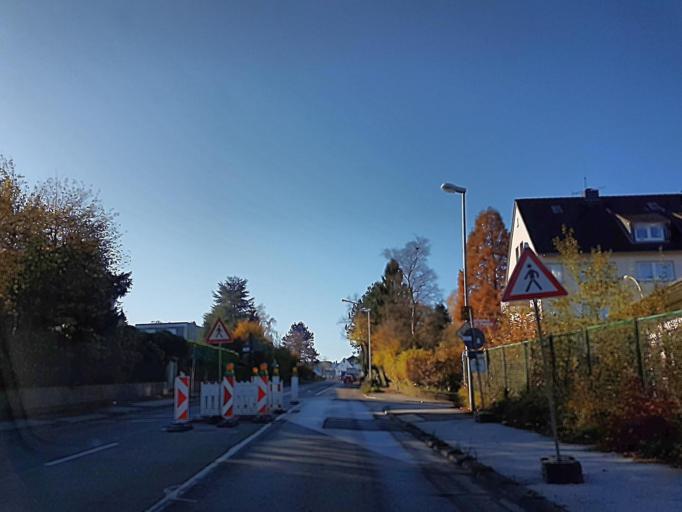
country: DE
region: North Rhine-Westphalia
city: Wermelskirchen
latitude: 51.1885
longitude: 7.2647
